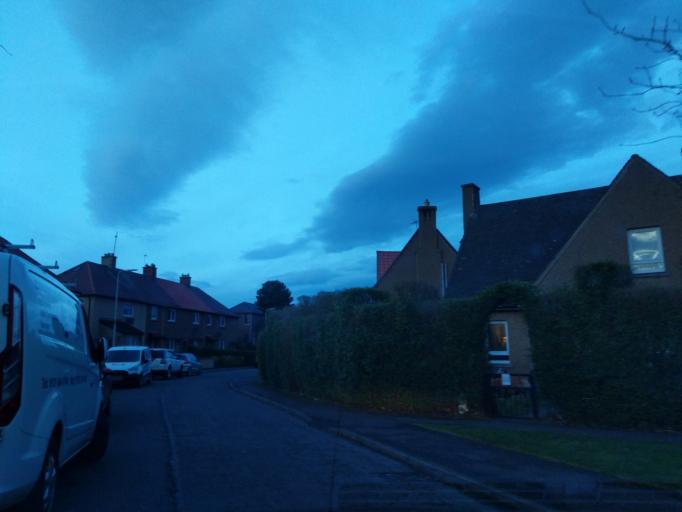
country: GB
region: Scotland
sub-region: Midlothian
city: Loanhead
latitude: 55.8670
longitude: -3.1827
